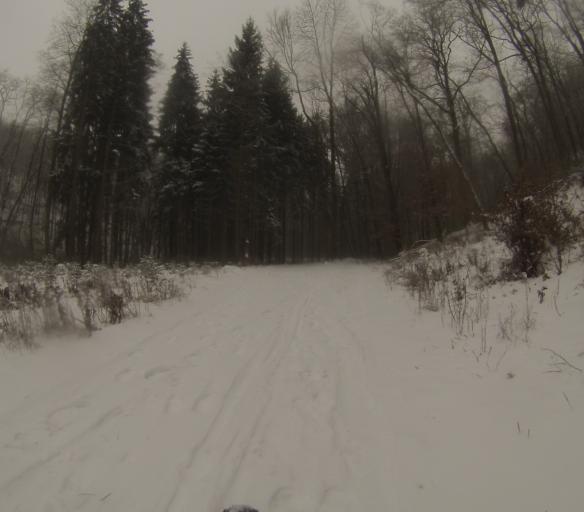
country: CZ
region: South Moravian
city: Strelice
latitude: 49.1331
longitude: 16.5111
